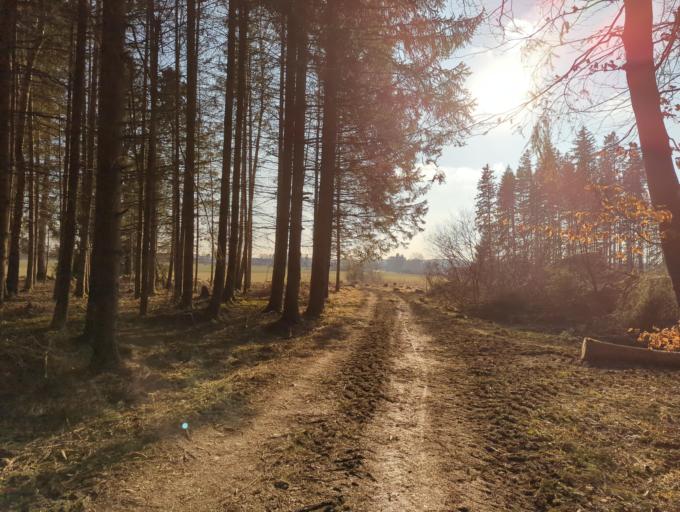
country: DE
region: Bavaria
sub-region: Swabia
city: Bad Worishofen
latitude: 47.9868
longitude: 10.5871
